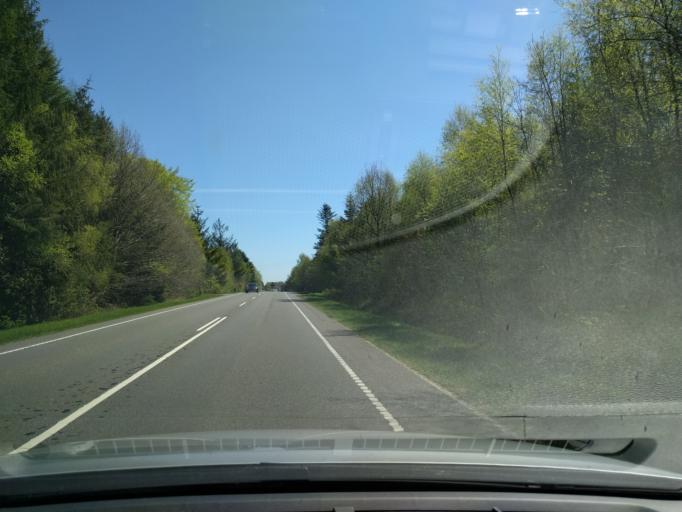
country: DK
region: South Denmark
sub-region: Billund Kommune
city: Billund
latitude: 55.6199
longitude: 9.1051
